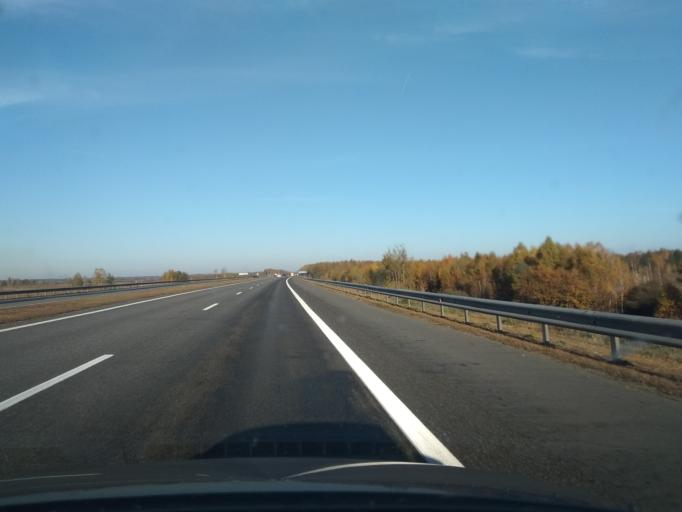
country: BY
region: Brest
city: Nyakhachava
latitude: 52.6067
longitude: 25.1668
